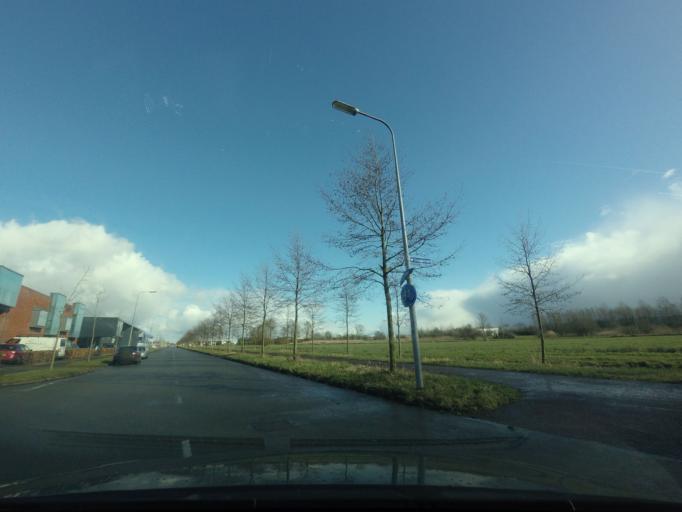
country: NL
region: Groningen
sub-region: Gemeente Groningen
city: Oosterpark
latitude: 53.2106
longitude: 6.6123
